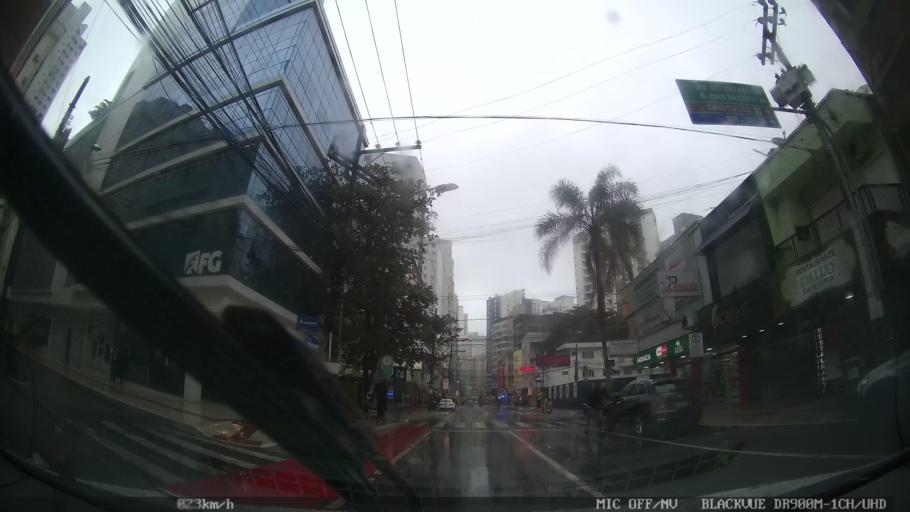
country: BR
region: Santa Catarina
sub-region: Balneario Camboriu
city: Balneario Camboriu
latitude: -26.9829
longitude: -48.6358
